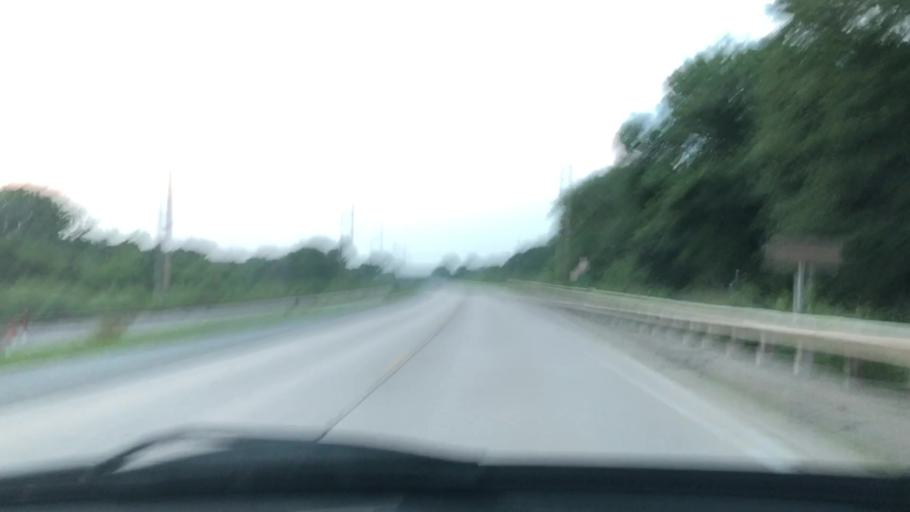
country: US
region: Iowa
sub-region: Johnson County
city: North Liberty
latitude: 41.7951
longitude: -91.6417
